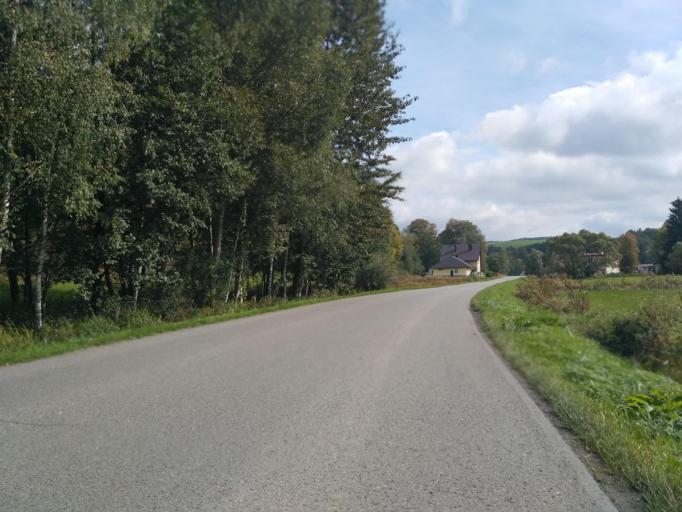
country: PL
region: Subcarpathian Voivodeship
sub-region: Powiat ropczycko-sedziszowski
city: Niedzwiada
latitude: 49.9328
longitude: 21.5507
